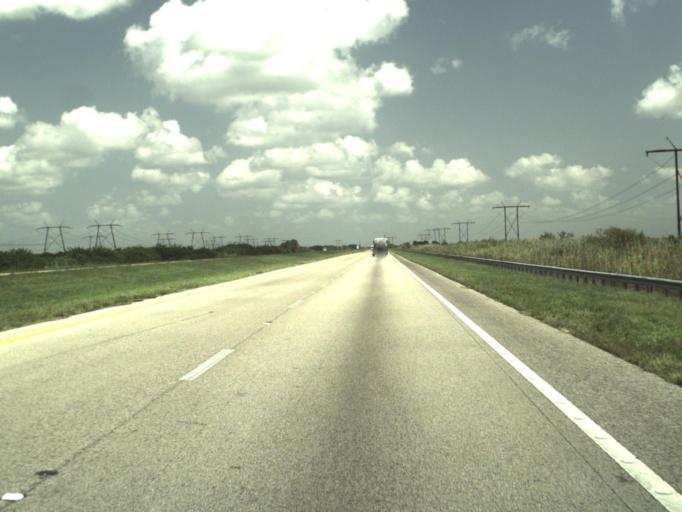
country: US
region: Florida
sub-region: Broward County
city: Weston
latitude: 26.2141
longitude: -80.4568
